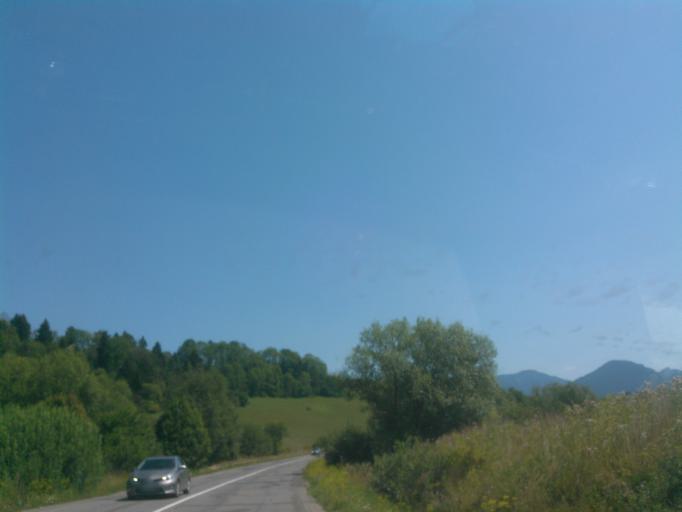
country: SK
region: Zilinsky
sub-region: Okres Liptovsky Mikulas
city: Liptovsky Mikulas
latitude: 49.0571
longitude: 19.5096
